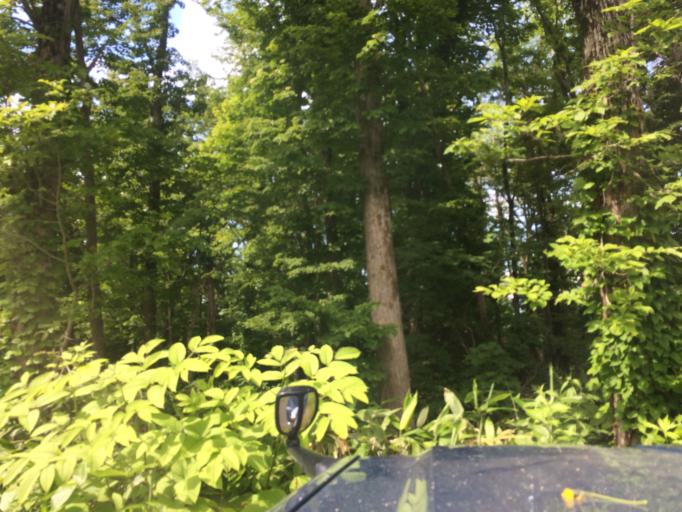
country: JP
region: Hokkaido
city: Niseko Town
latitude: 42.8652
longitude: 140.8002
